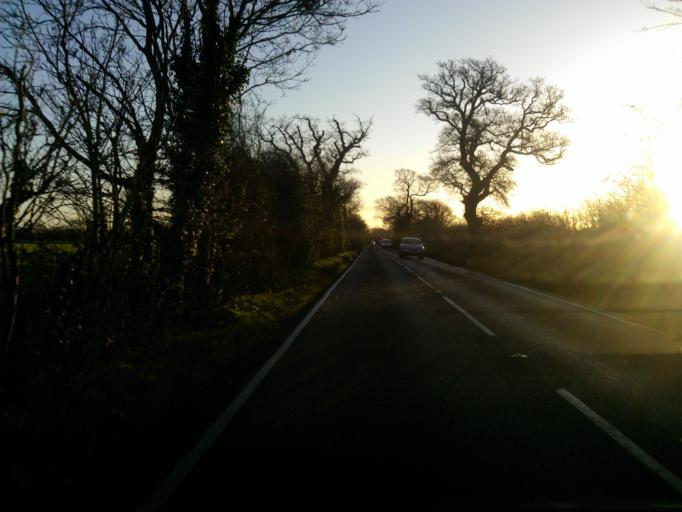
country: GB
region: England
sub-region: Essex
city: Wivenhoe
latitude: 51.8760
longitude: 0.9652
